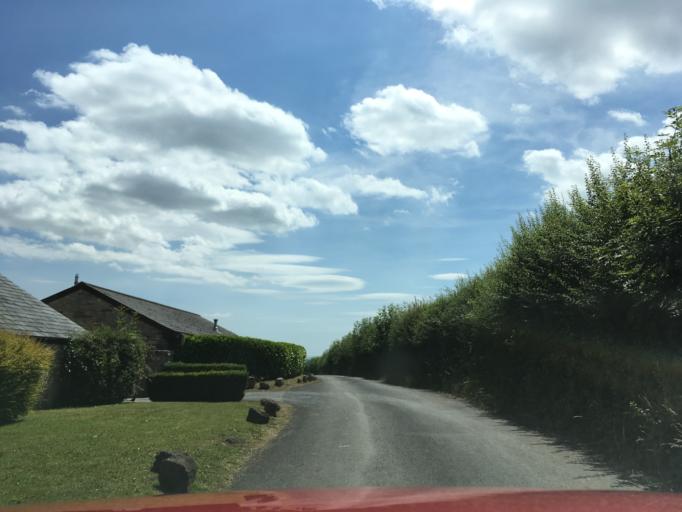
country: GB
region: Wales
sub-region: Newport
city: Langstone
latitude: 51.6008
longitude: -2.9109
